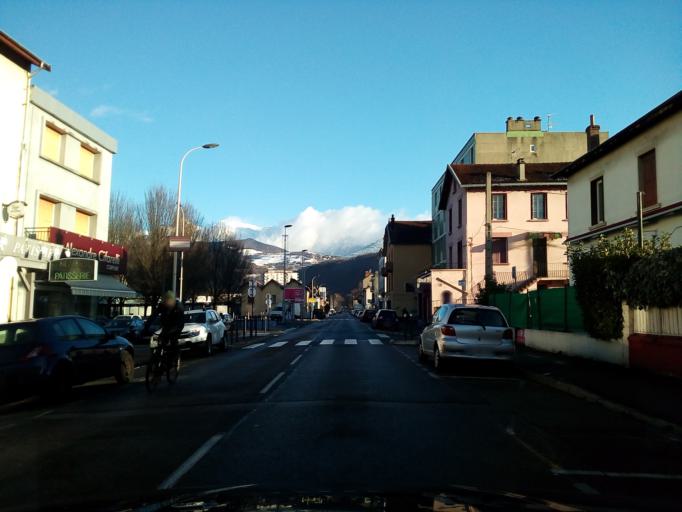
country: FR
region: Rhone-Alpes
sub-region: Departement de l'Isere
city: Saint-Martin-d'Heres
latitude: 45.1824
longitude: 5.7596
